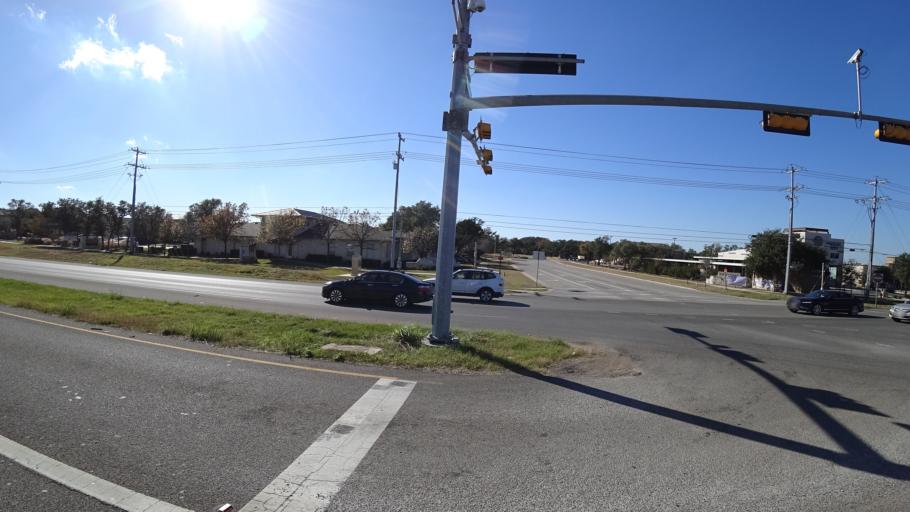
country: US
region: Texas
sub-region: Williamson County
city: Brushy Creek
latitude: 30.5229
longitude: -97.7744
